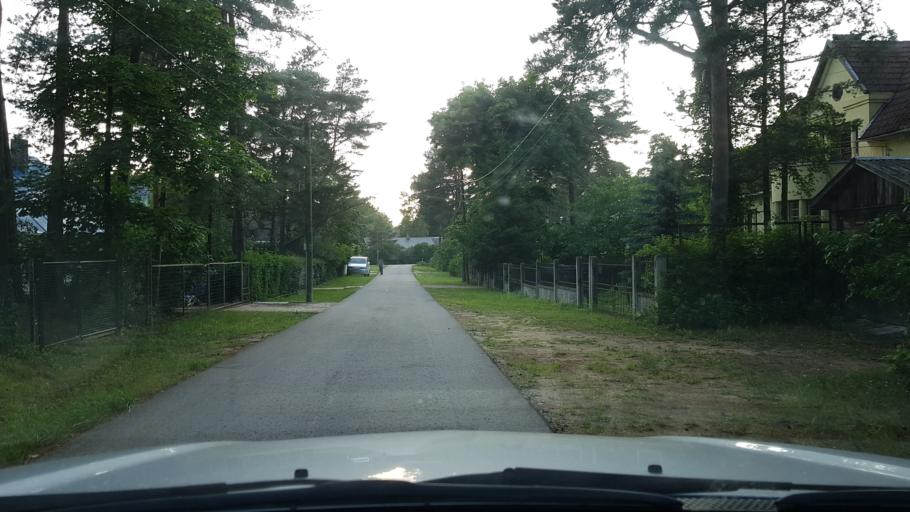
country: EE
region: Ida-Virumaa
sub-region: Narva-Joesuu linn
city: Narva-Joesuu
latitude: 59.4552
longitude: 28.0513
